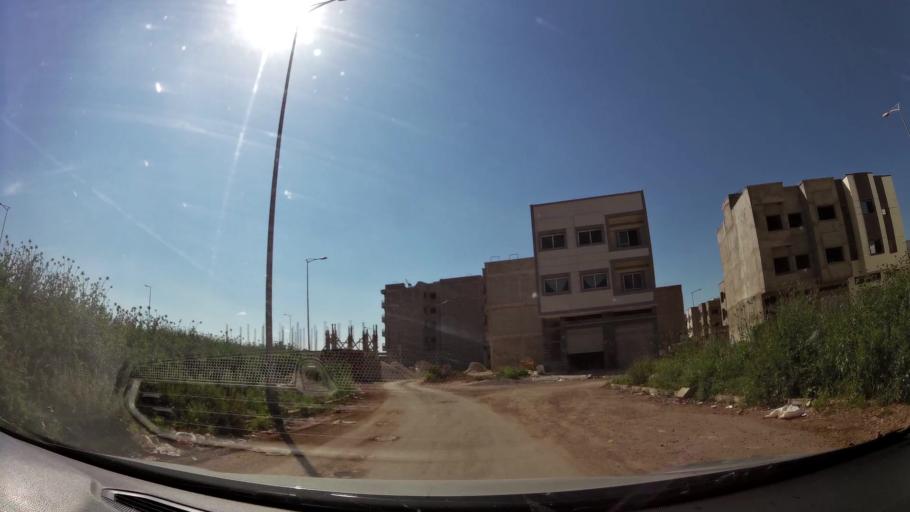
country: MA
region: Fes-Boulemane
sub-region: Fes
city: Fes
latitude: 33.9923
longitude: -5.0077
